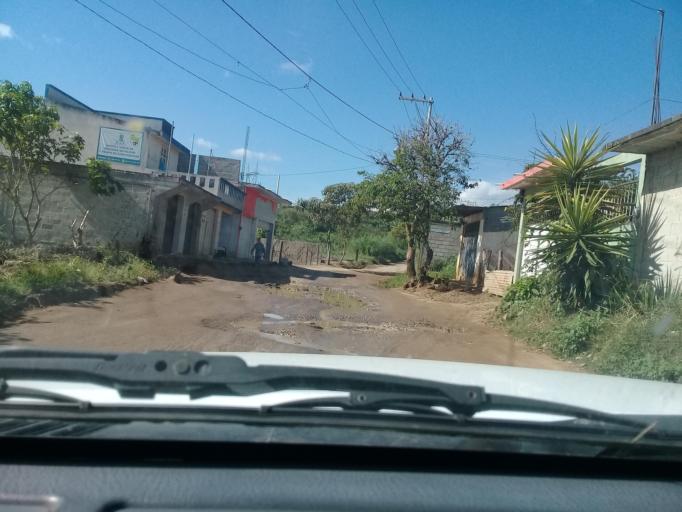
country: MX
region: Veracruz
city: El Castillo
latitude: 19.5634
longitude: -96.8841
